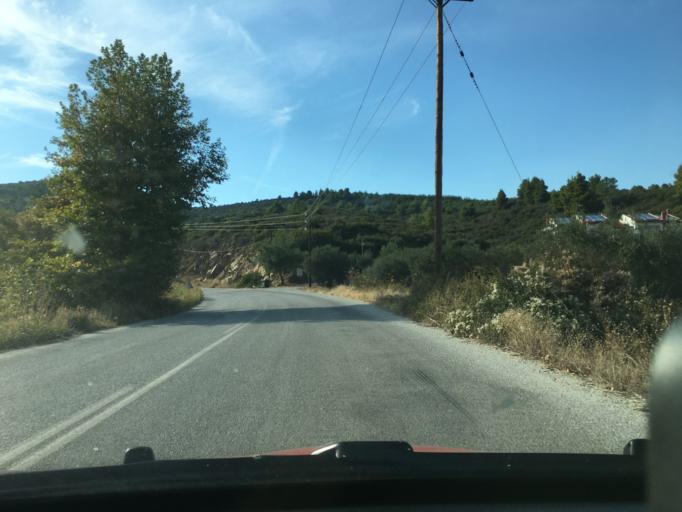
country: GR
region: Central Macedonia
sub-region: Nomos Chalkidikis
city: Agios Nikolaos
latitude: 40.2941
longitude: 23.6878
